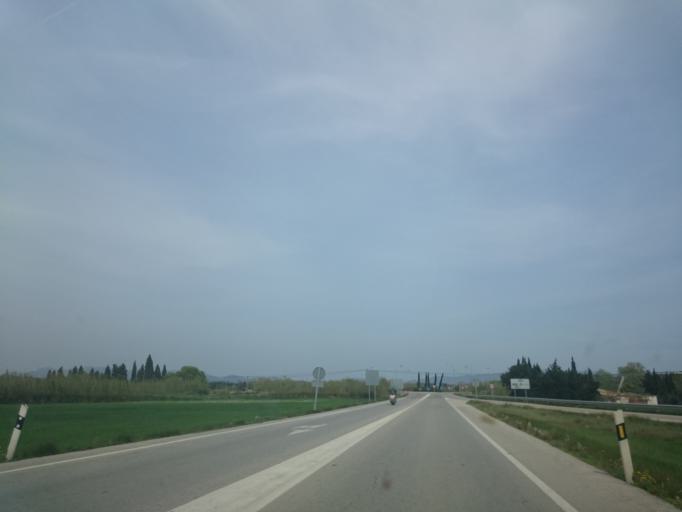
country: ES
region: Catalonia
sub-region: Provincia de Girona
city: Vilabertran
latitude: 42.2764
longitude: 2.9853
